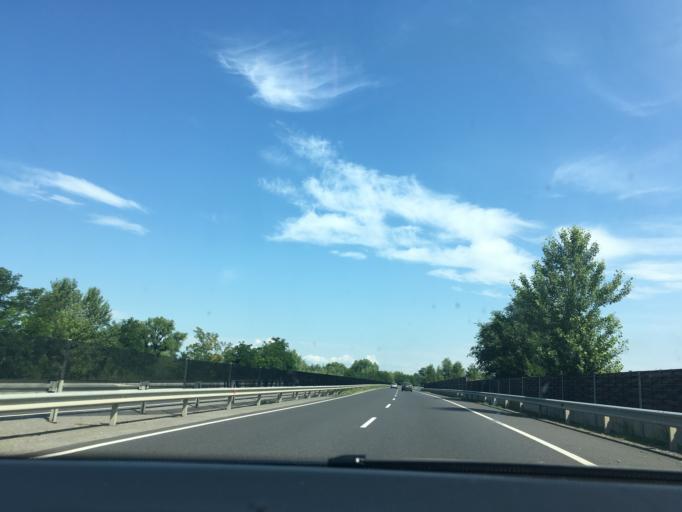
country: HU
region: Szabolcs-Szatmar-Bereg
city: Nyiregyhaza
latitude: 47.8895
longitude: 21.7106
